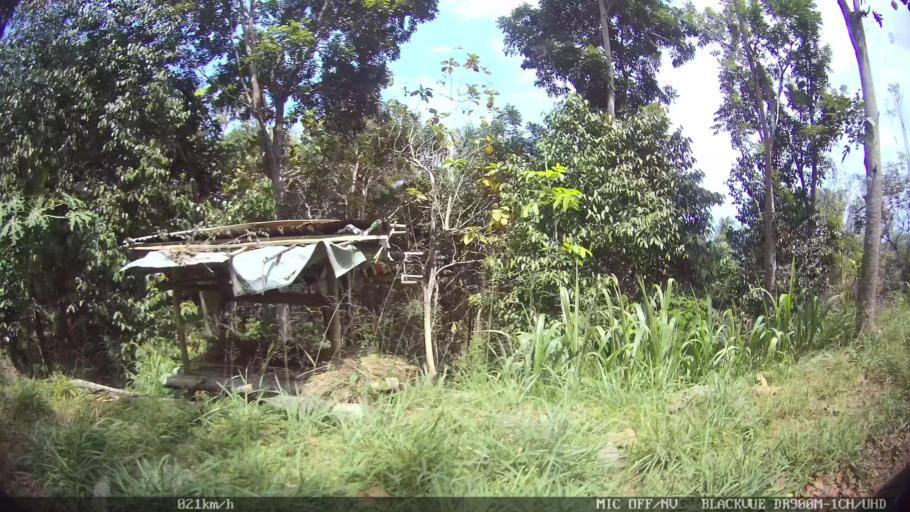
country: ID
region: Central Java
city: Candi Prambanan
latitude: -7.8131
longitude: 110.5244
